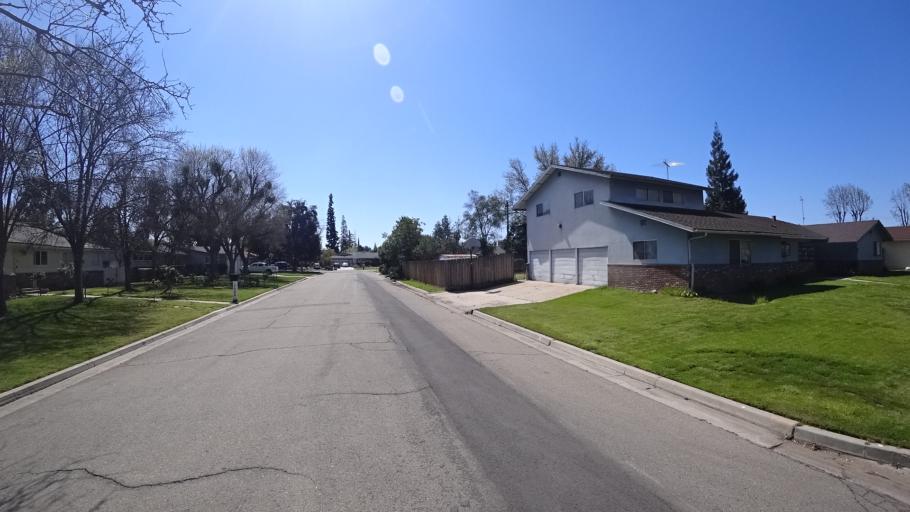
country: US
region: California
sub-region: Fresno County
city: Fresno
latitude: 36.8102
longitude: -119.7933
